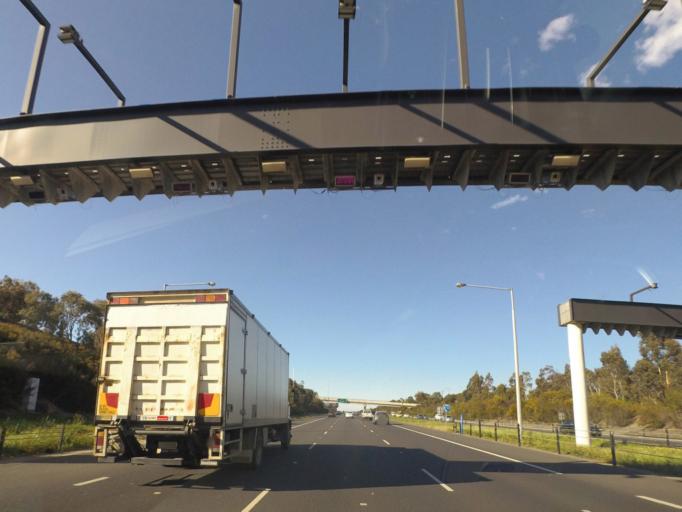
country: AU
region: Victoria
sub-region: Knox
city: Wantirna South
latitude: -37.8864
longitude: 145.2151
